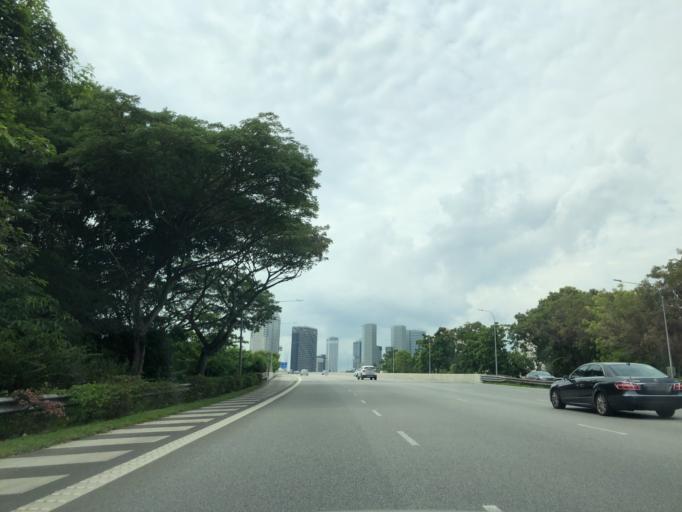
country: SG
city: Singapore
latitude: 1.2951
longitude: 103.8713
